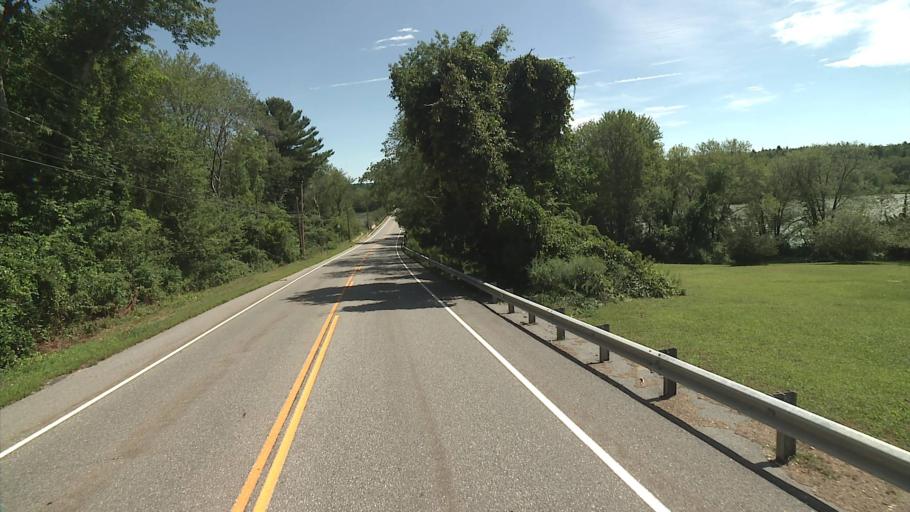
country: US
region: Rhode Island
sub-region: Providence County
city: Foster
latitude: 41.8490
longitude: -71.8133
